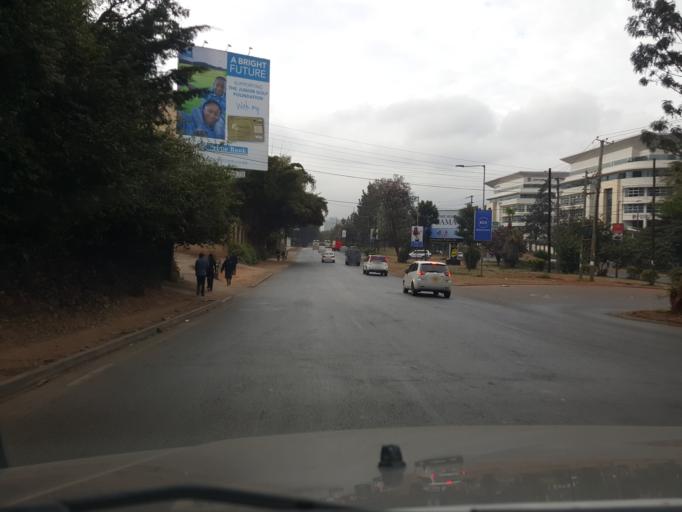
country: KE
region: Nairobi Area
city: Nairobi
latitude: -1.2676
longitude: 36.8050
